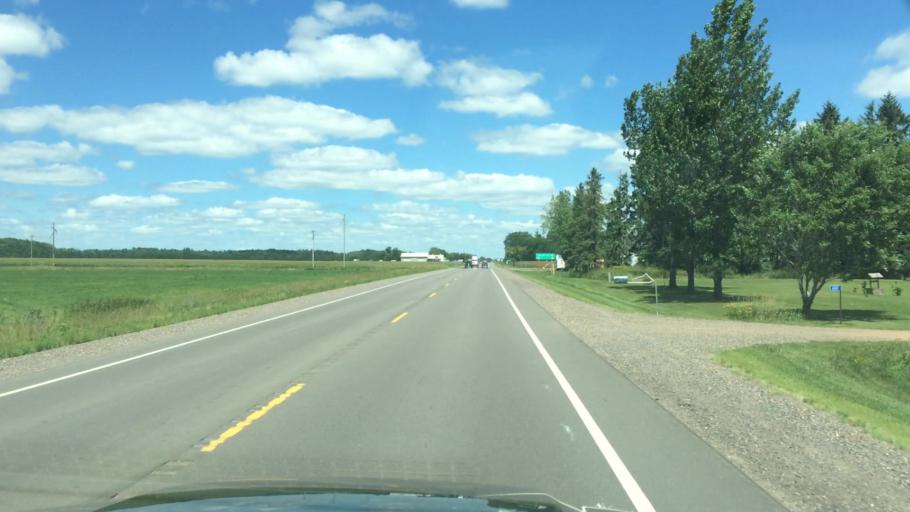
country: US
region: Wisconsin
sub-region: Clark County
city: Abbotsford
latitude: 45.0315
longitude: -90.3150
